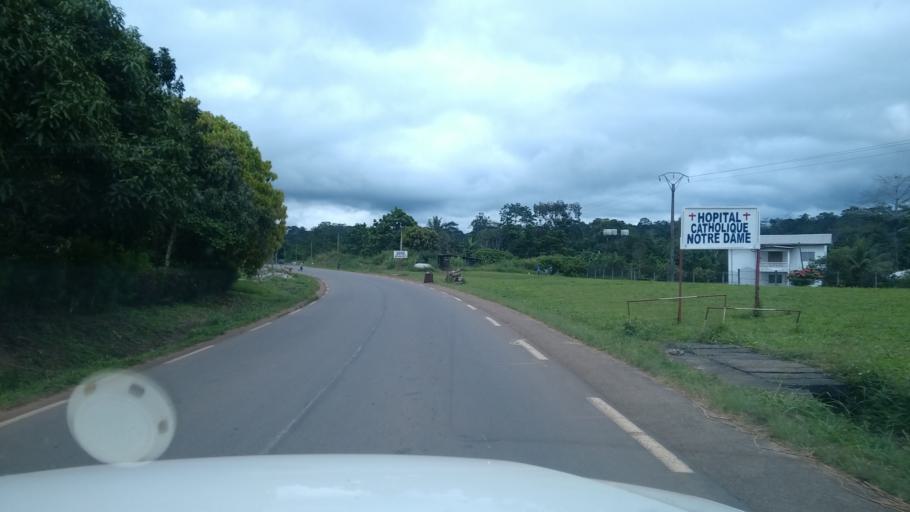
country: CM
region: Centre
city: Mbalmayo
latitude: 3.5976
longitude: 11.5242
